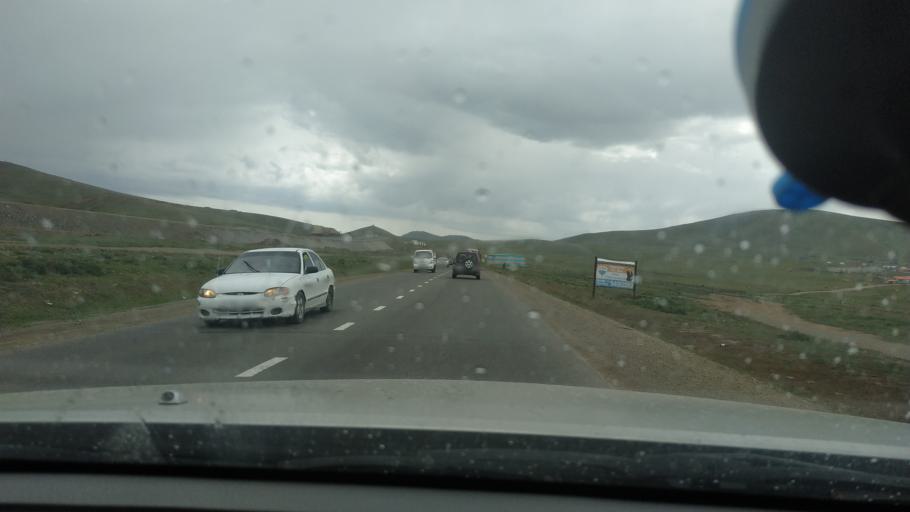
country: MN
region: Ulaanbaatar
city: Ulaanbaatar
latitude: 47.7998
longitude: 106.7463
